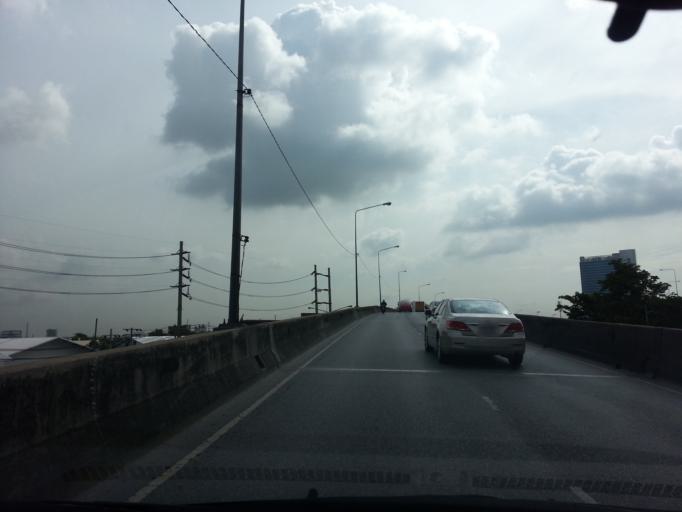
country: TH
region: Bangkok
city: Huai Khwang
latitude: 13.7548
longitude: 100.5792
